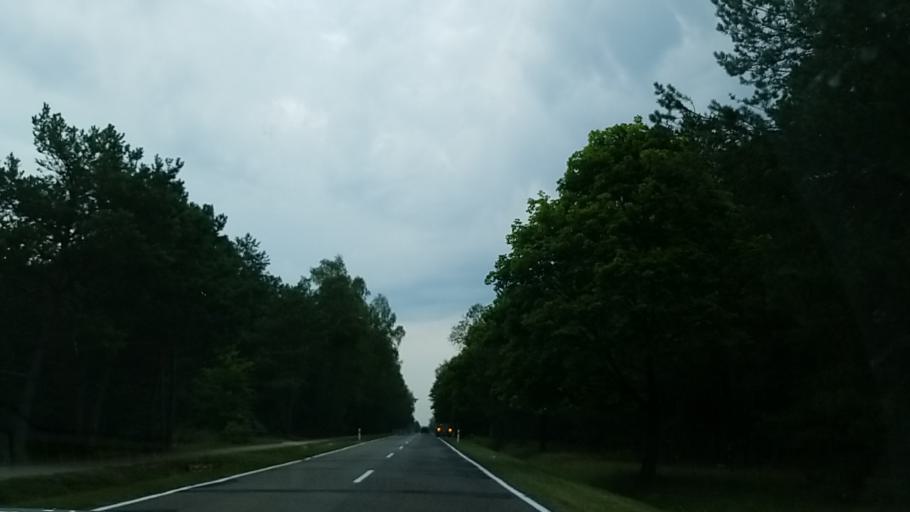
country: PL
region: Lublin Voivodeship
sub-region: Powiat bialski
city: Slawatycze
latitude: 51.7257
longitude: 23.5121
